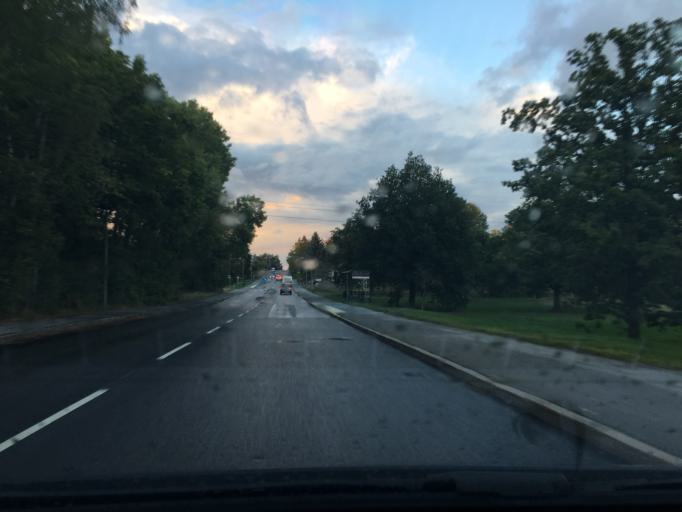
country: SE
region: Stockholm
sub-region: Jarfalla Kommun
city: Jakobsberg
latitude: 59.3733
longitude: 17.8681
